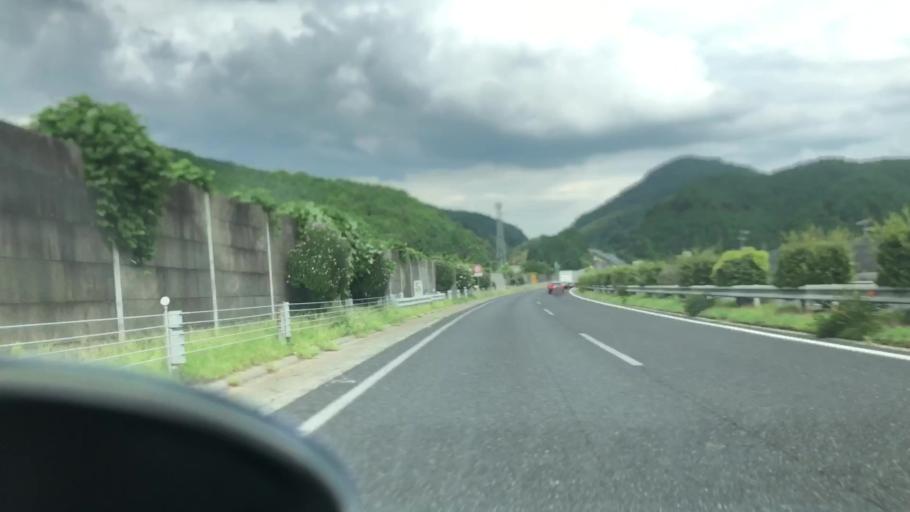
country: JP
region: Hyogo
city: Yamazakicho-nakabirose
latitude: 34.9785
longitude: 134.6307
